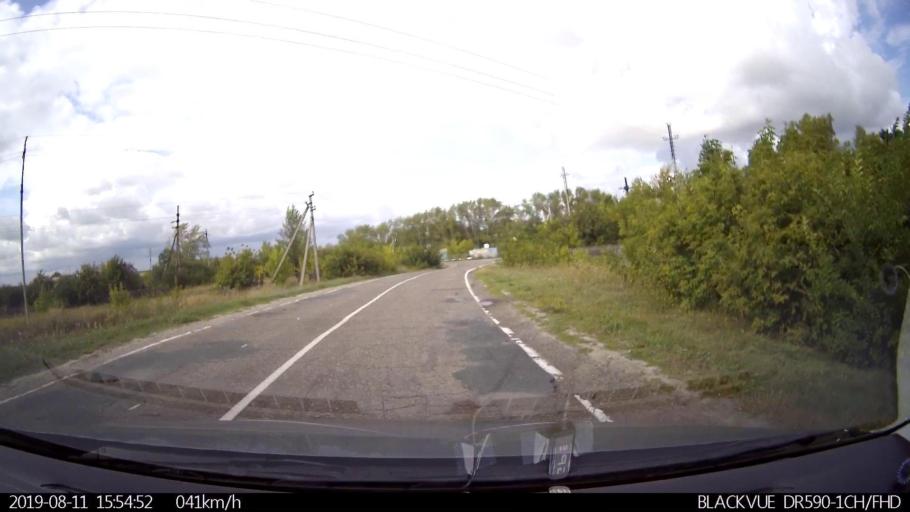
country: RU
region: Ulyanovsk
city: Ignatovka
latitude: 53.9435
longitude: 47.6560
